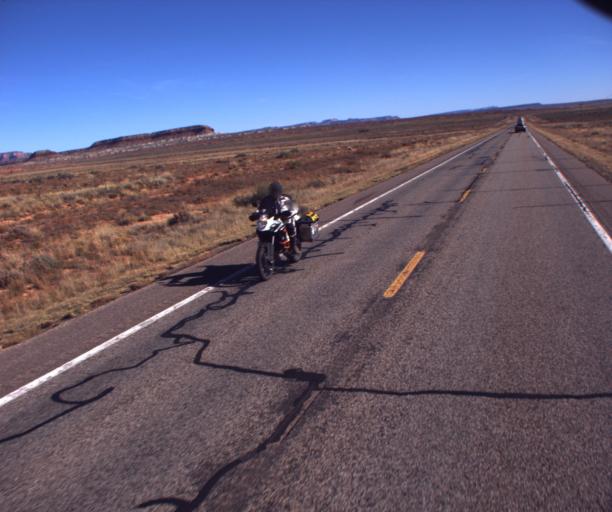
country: US
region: Arizona
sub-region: Coconino County
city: Fredonia
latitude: 36.8910
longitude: -112.6198
